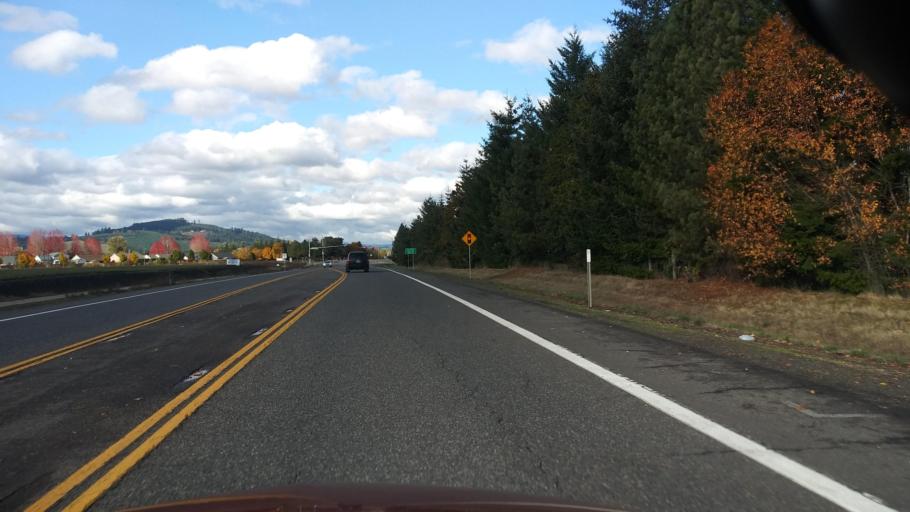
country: US
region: Oregon
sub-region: Washington County
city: Forest Grove
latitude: 45.5335
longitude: -123.1035
